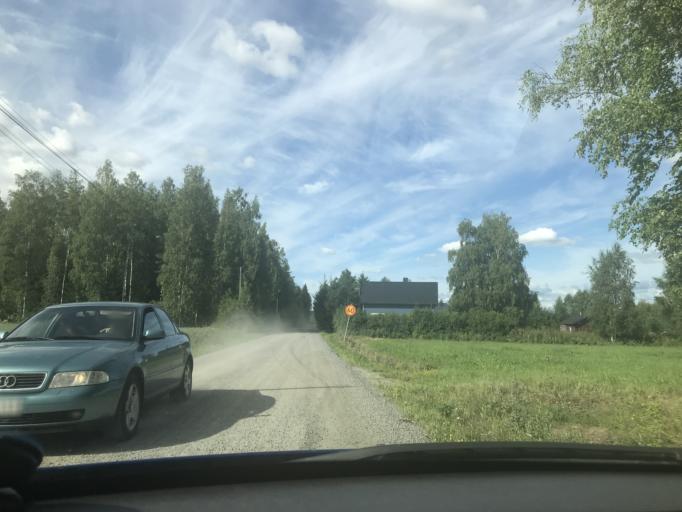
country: FI
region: Southern Ostrobothnia
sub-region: Kuusiokunnat
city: Alavus
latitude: 62.5895
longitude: 23.5827
